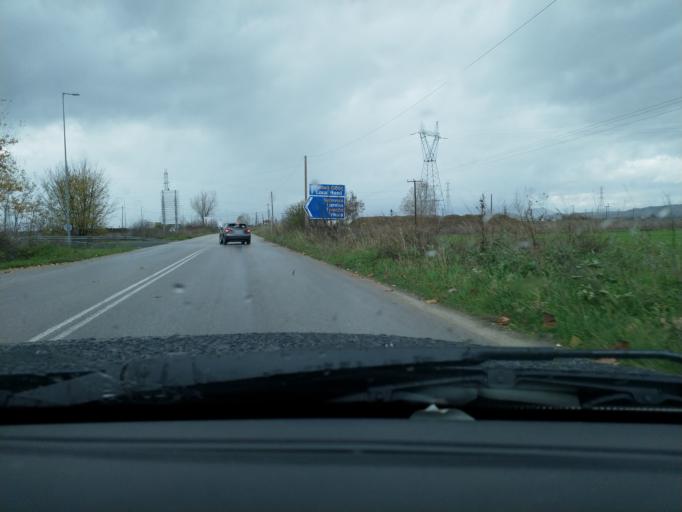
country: GR
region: Thessaly
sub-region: Trikala
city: Taxiarches
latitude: 39.5633
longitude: 21.8865
